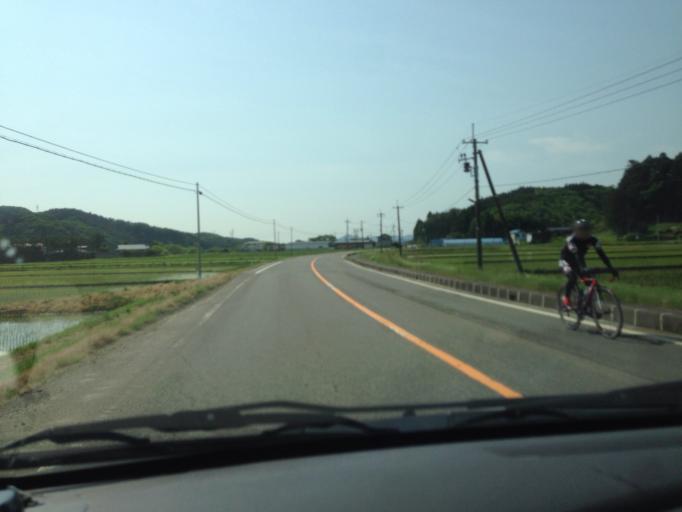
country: JP
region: Tochigi
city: Kuroiso
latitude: 37.1657
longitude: 140.1727
